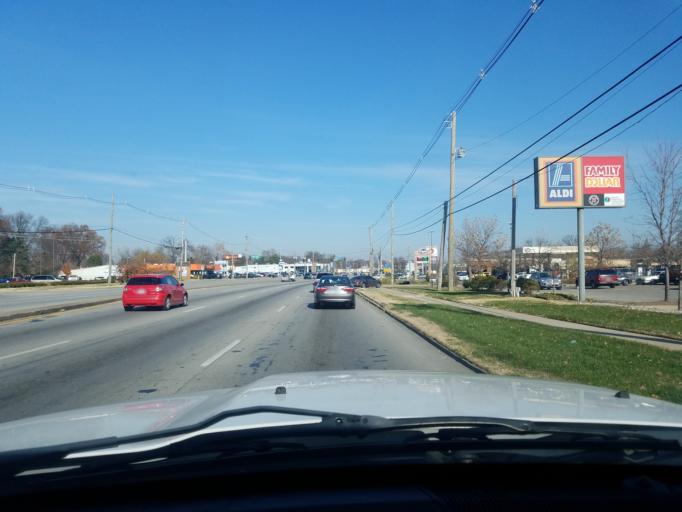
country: US
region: Kentucky
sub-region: Jefferson County
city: Saint Dennis
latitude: 38.1672
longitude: -85.8290
